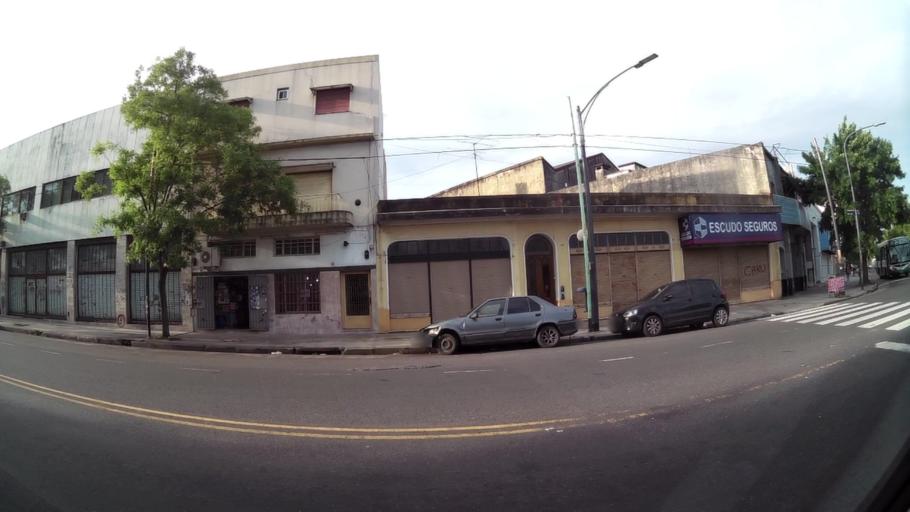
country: AR
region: Buenos Aires F.D.
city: Buenos Aires
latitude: -34.6449
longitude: -58.4257
